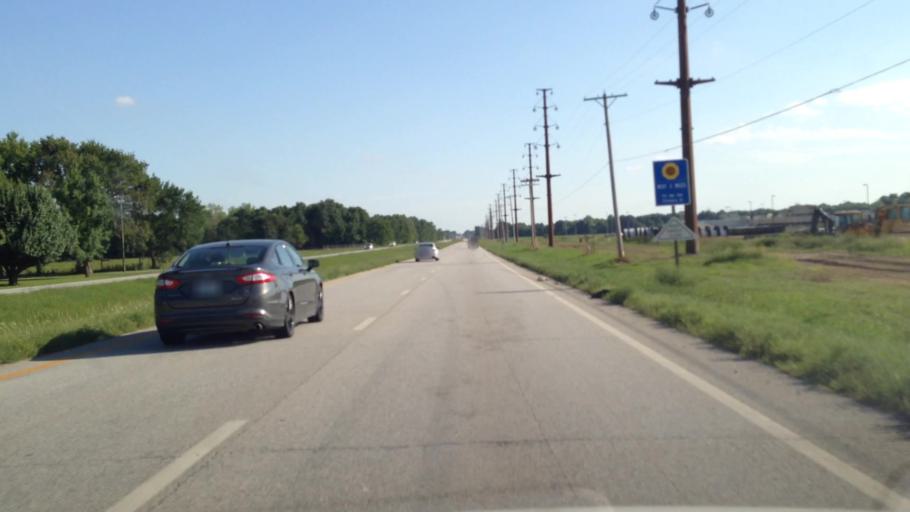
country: US
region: Kansas
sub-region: Crawford County
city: Frontenac
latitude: 37.4841
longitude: -94.7053
